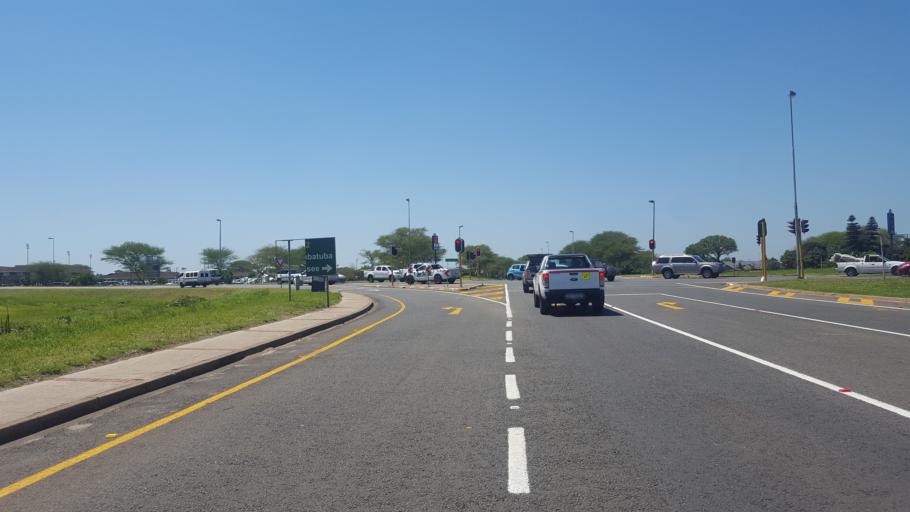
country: ZA
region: KwaZulu-Natal
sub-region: uThungulu District Municipality
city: Richards Bay
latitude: -28.7511
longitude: 32.0552
